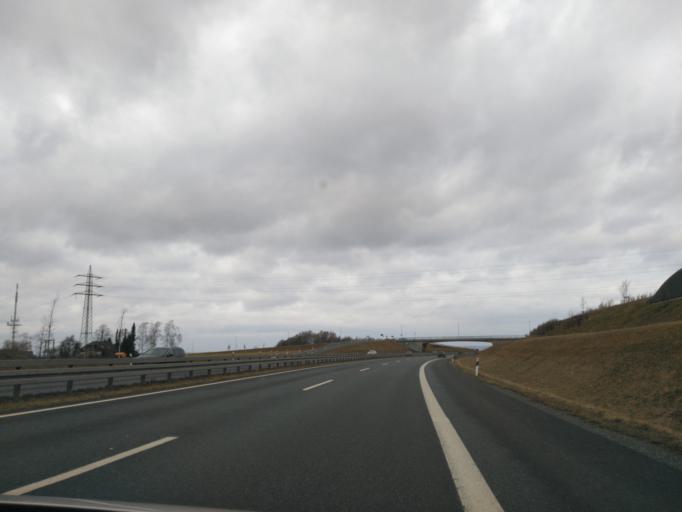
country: DE
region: Saxony
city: Hilbersdorf
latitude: 50.7986
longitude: 12.9760
